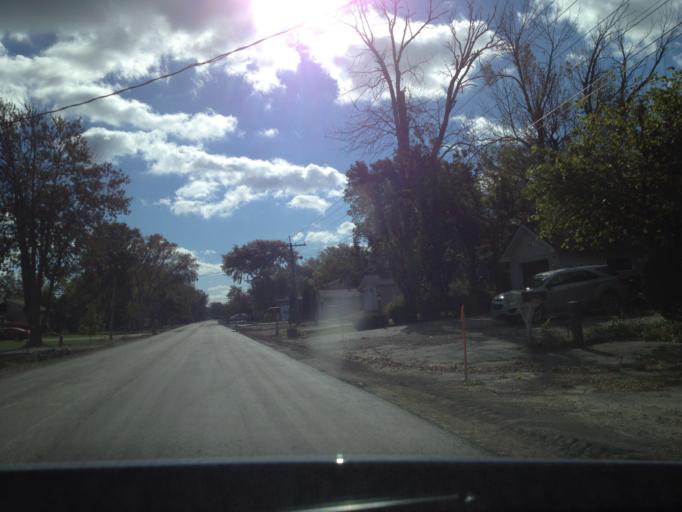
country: CA
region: Ontario
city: Amherstburg
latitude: 42.0017
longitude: -82.5631
